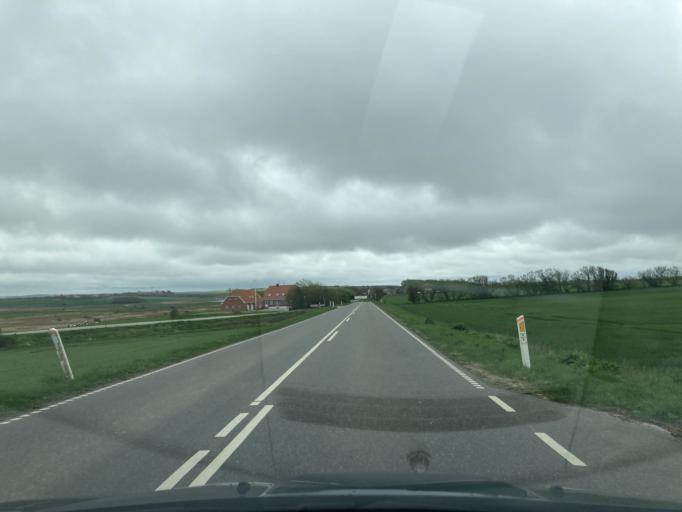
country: DK
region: North Denmark
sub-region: Thisted Kommune
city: Hurup
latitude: 56.8200
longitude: 8.3504
